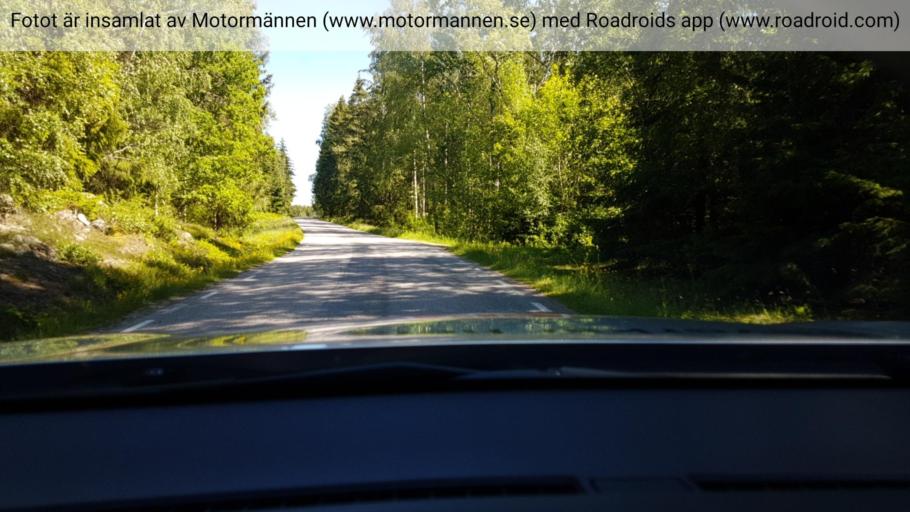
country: SE
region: Vaestra Goetaland
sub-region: Toreboda Kommun
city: Toereboda
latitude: 58.8129
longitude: 14.0471
